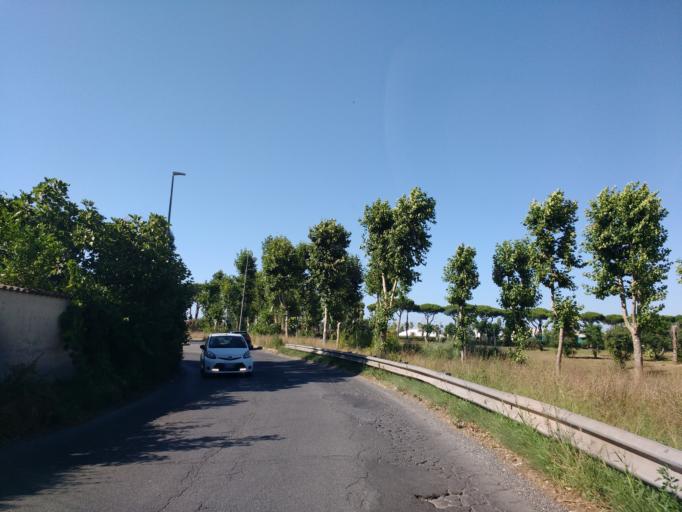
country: IT
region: Latium
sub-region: Citta metropolitana di Roma Capitale
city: Acilia-Castel Fusano-Ostia Antica
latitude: 41.7498
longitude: 12.3304
